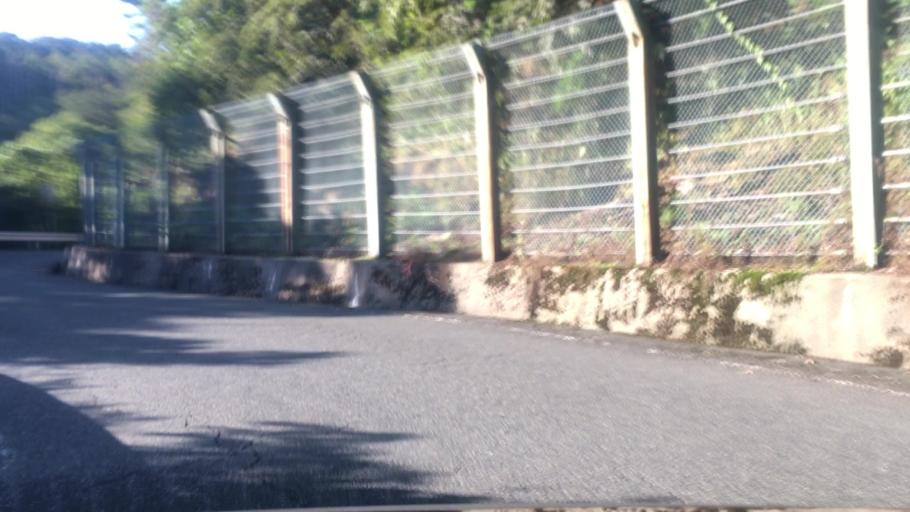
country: JP
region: Hyogo
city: Toyooka
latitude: 35.6161
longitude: 134.8750
